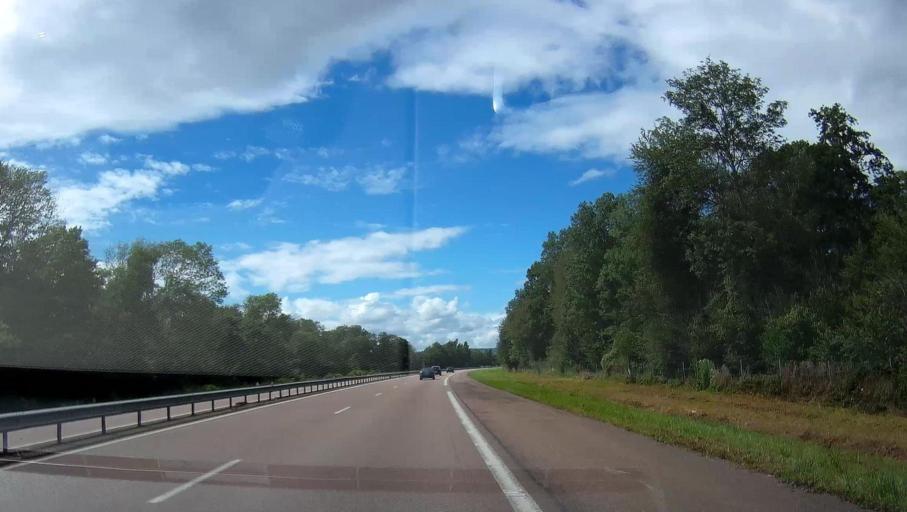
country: FR
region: Bourgogne
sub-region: Departement de la Cote-d'Or
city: Fenay
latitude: 47.2437
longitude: 5.0738
